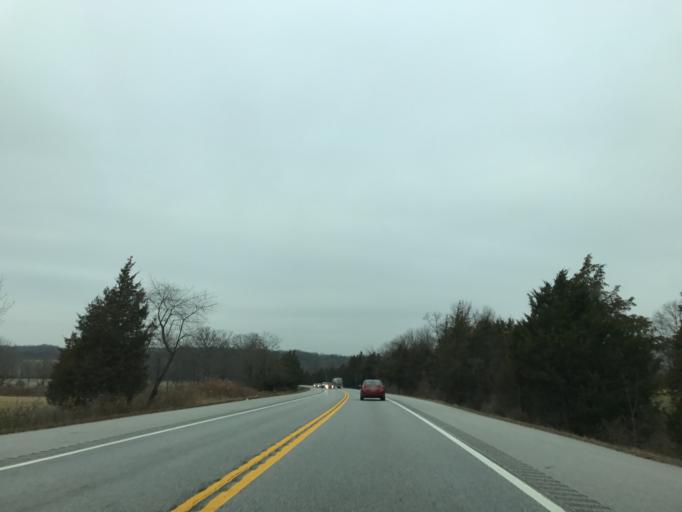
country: US
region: Maryland
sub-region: Carroll County
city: Taneytown
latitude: 39.6437
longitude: -77.1299
